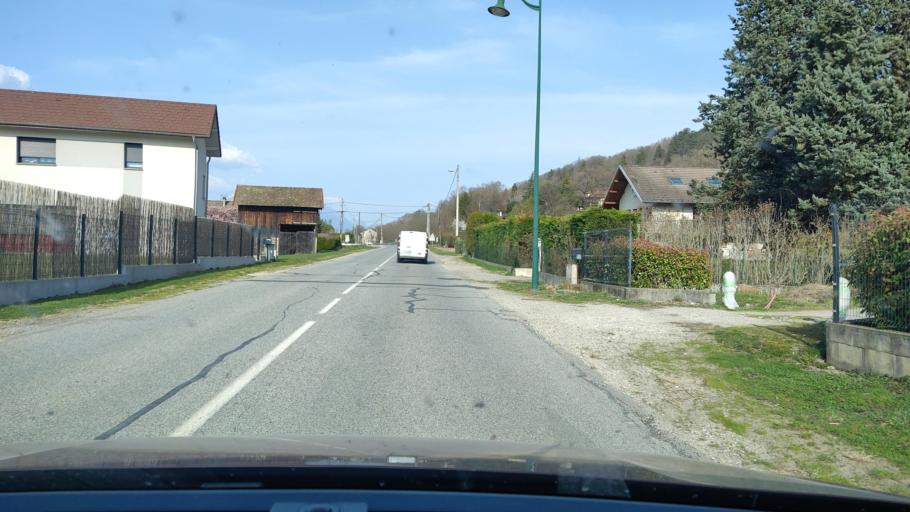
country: FR
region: Rhone-Alpes
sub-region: Departement de l'Isere
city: Pontcharra
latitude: 45.4500
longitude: 6.0406
